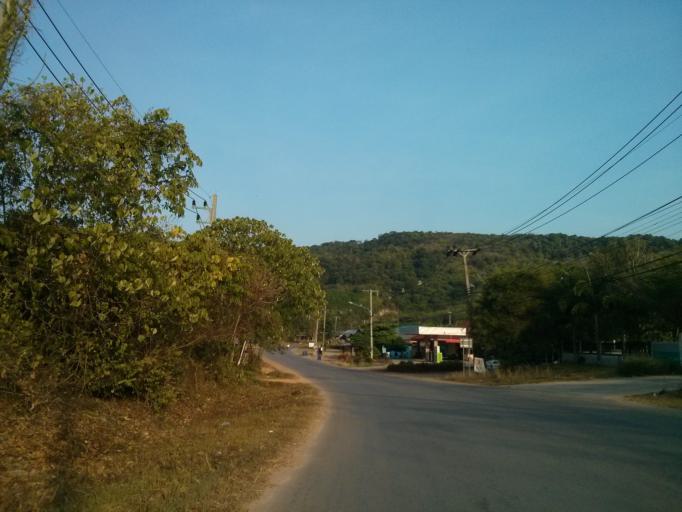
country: TH
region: Krabi
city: Saladan
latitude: 7.5678
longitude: 99.0380
